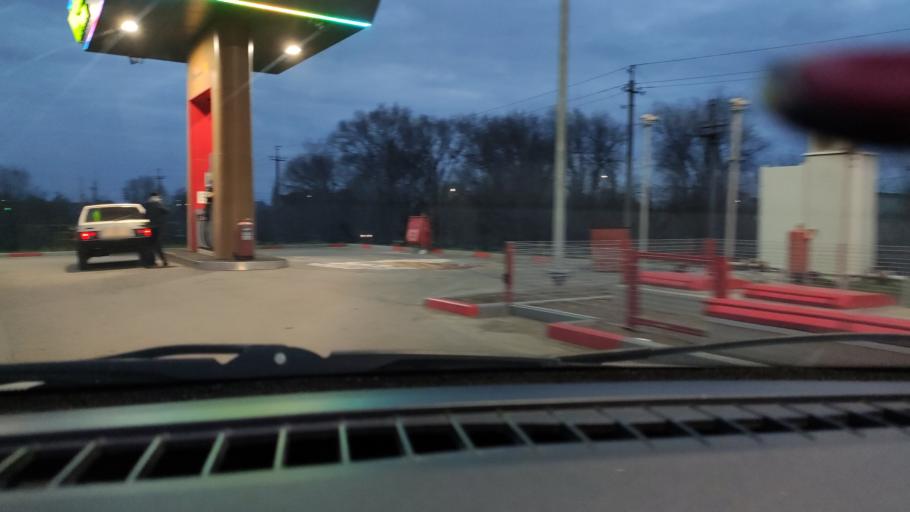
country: RU
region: Orenburg
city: Tatarskaya Kargala
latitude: 51.8708
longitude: 55.1439
